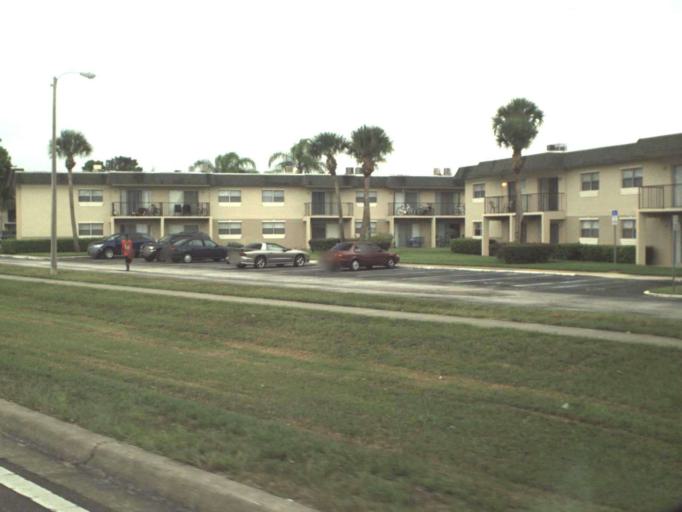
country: US
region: Florida
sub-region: Seminole County
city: Goldenrod
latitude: 28.6104
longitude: -81.3089
